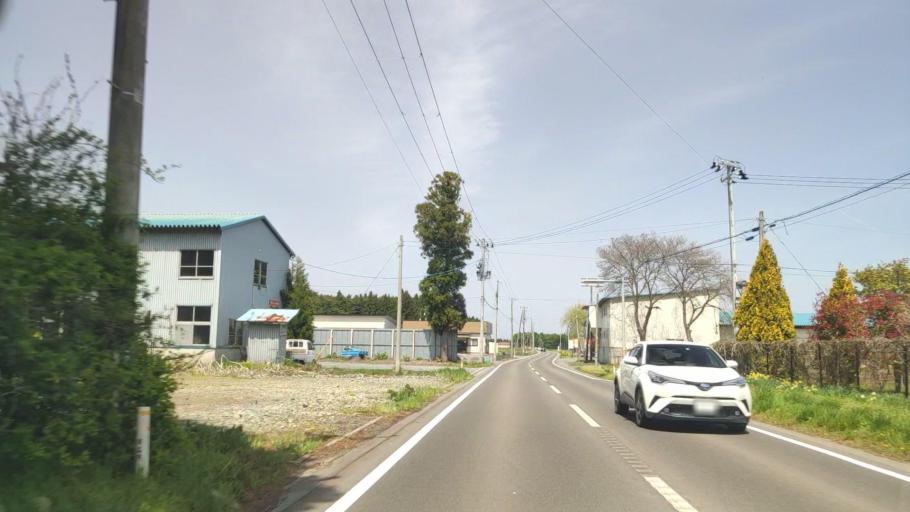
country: JP
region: Aomori
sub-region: Hachinohe Shi
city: Uchimaru
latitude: 40.5369
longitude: 141.4018
